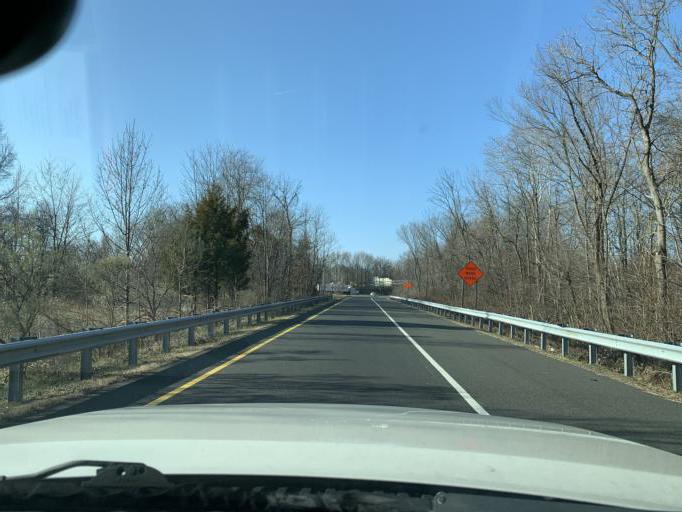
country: US
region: Maryland
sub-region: Prince George's County
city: Largo
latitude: 38.8939
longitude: -76.8456
